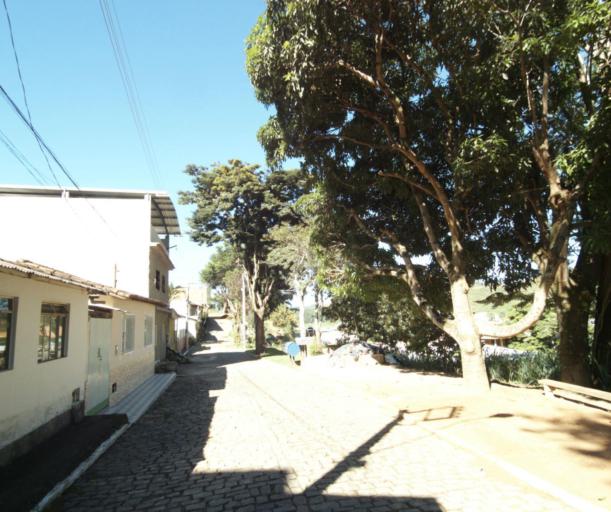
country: BR
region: Minas Gerais
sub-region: Espera Feliz
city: Espera Feliz
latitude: -20.6912
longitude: -41.8477
